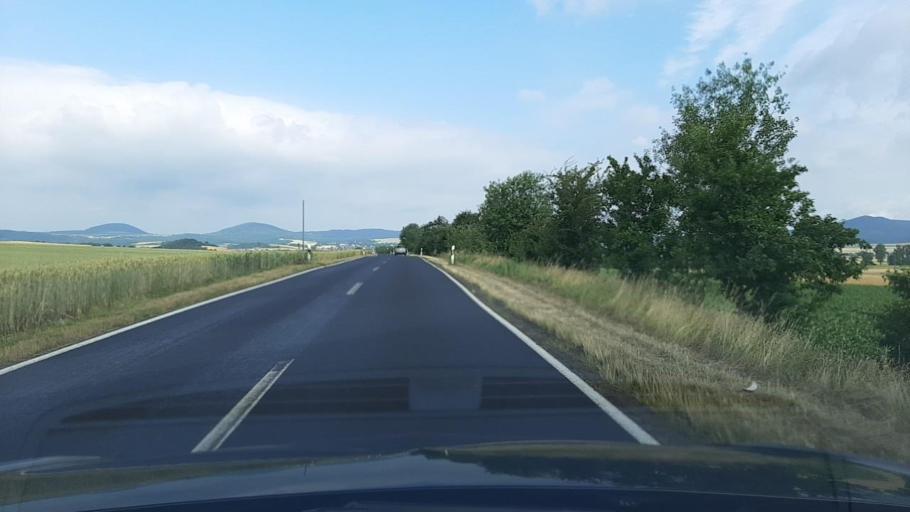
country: DE
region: Rheinland-Pfalz
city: Welling
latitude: 50.3502
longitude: 7.3354
